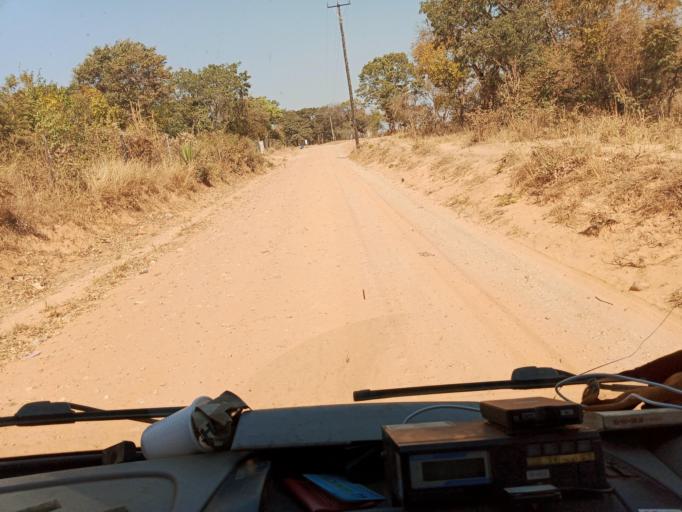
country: ZM
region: Lusaka
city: Lusaka
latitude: -15.3390
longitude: 28.1915
